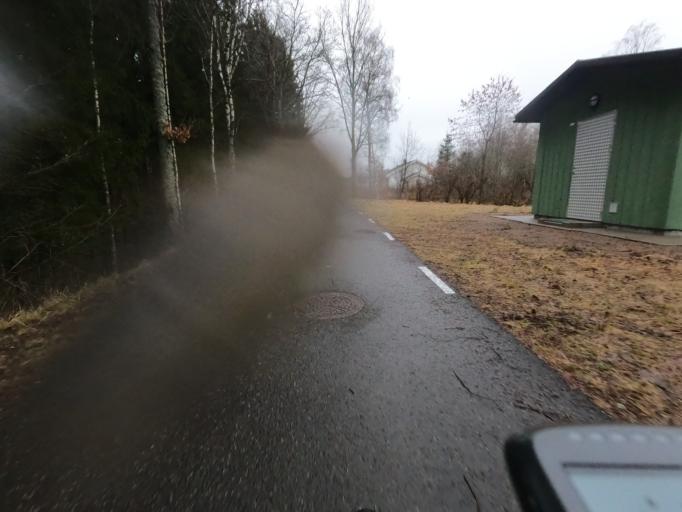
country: SE
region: Halland
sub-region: Halmstads Kommun
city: Aled
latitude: 56.7052
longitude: 13.0292
